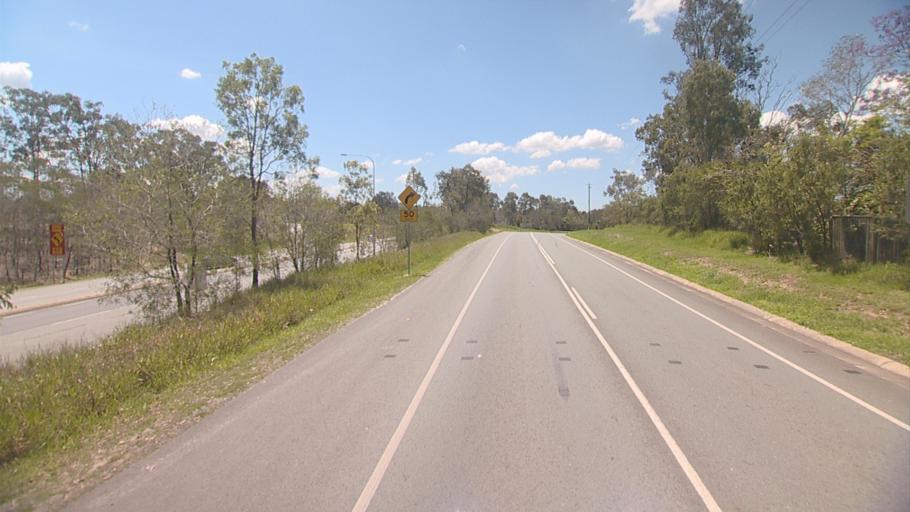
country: AU
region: Queensland
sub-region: Logan
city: Park Ridge South
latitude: -27.7276
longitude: 153.0300
